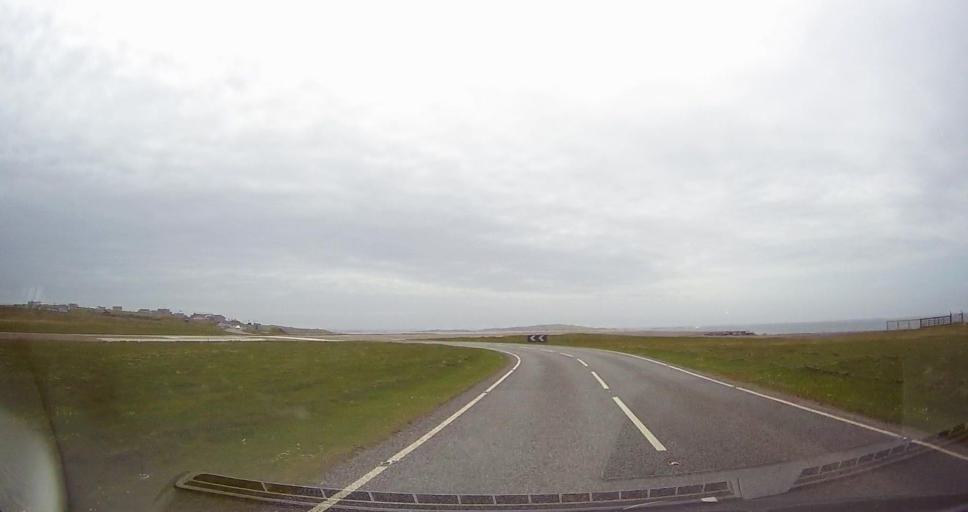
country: GB
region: Scotland
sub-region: Shetland Islands
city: Sandwick
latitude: 59.8820
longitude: -1.3039
